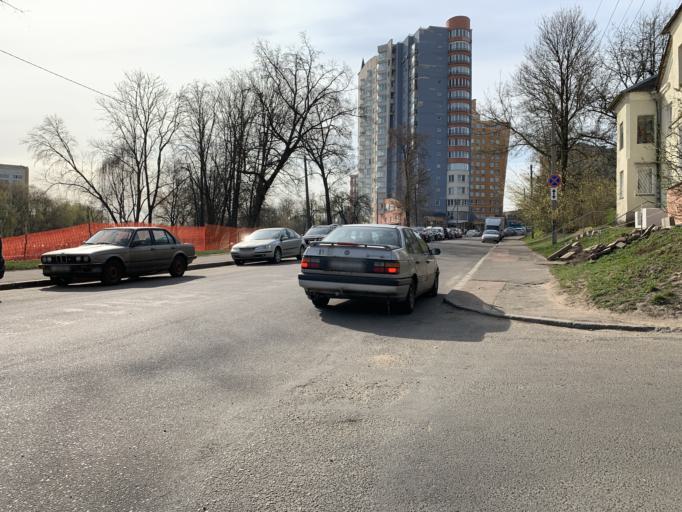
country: BY
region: Minsk
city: Minsk
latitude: 53.8923
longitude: 27.5621
